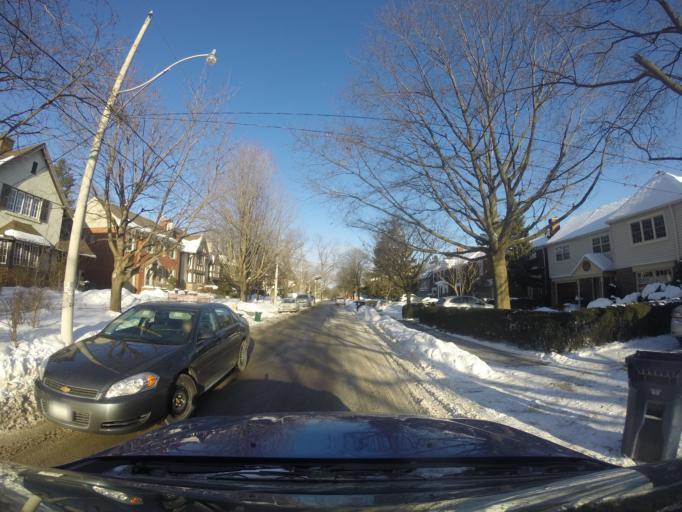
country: CA
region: Ontario
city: Toronto
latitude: 43.7229
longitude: -79.3932
